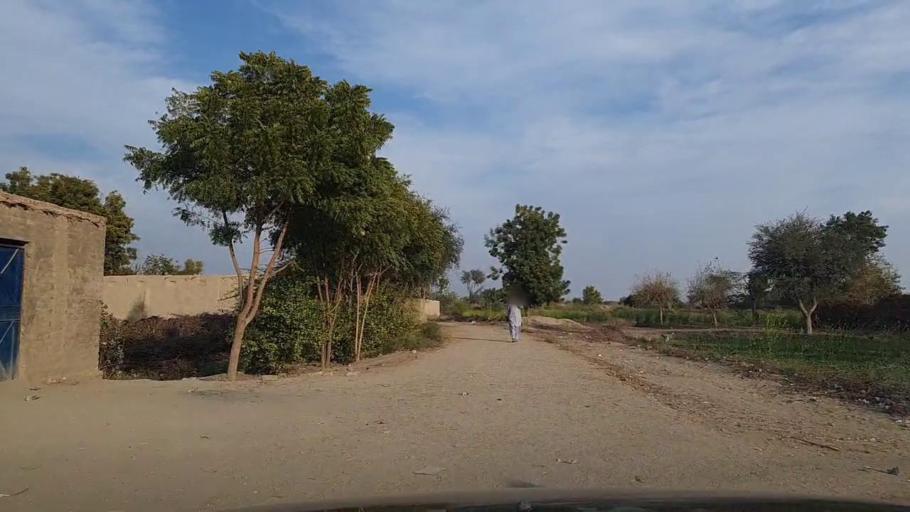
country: PK
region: Sindh
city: Jam Sahib
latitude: 26.4619
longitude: 68.5764
